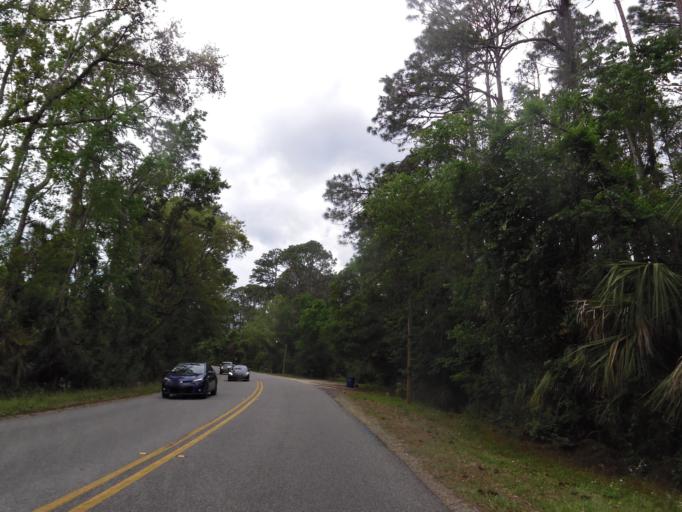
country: US
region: Florida
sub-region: Saint Johns County
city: Ponte Vedra Beach
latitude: 30.2272
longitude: -81.3943
